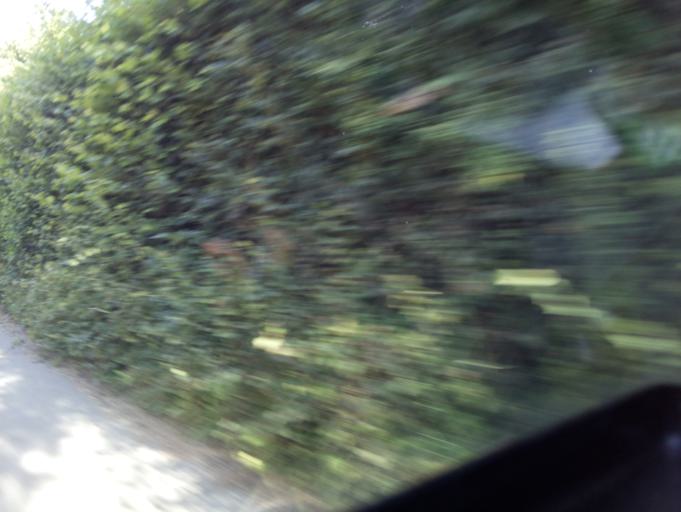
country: GB
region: England
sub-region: South Gloucestershire
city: Bitton
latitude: 51.4342
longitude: -2.4211
